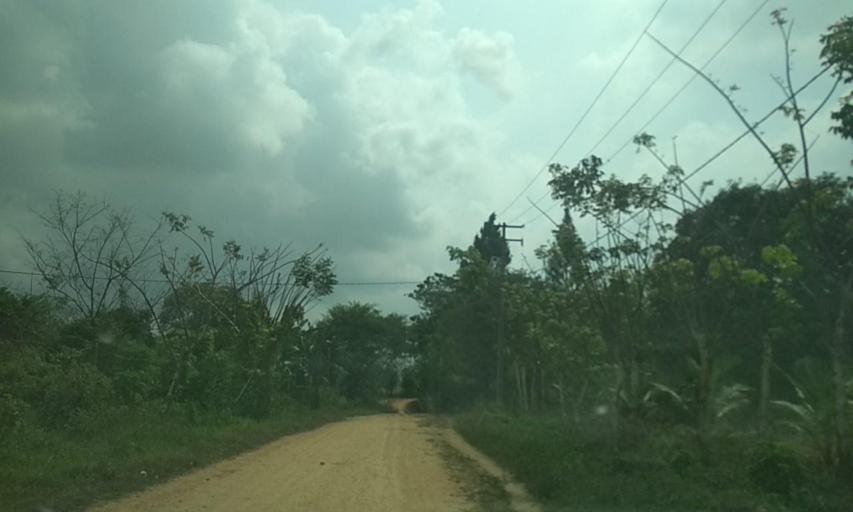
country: MX
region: Tabasco
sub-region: Huimanguillo
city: Francisco Rueda
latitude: 17.6549
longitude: -93.7529
